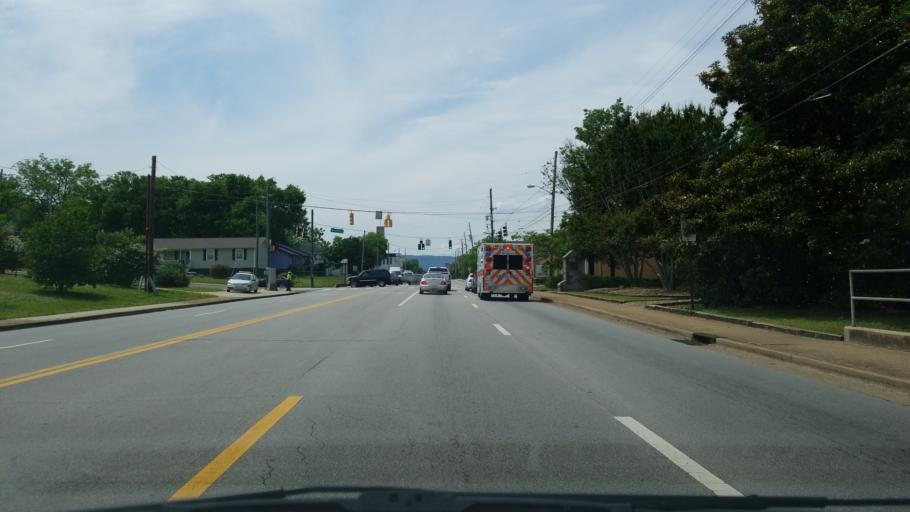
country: US
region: Tennessee
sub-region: Hamilton County
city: East Ridge
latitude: 35.0406
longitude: -85.2712
